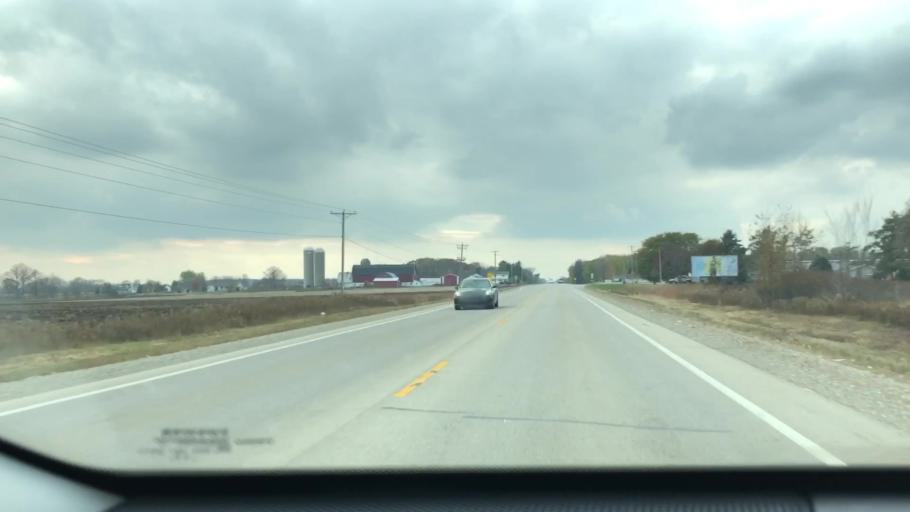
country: US
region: Wisconsin
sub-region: Outagamie County
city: Seymour
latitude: 44.5018
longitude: -88.2631
